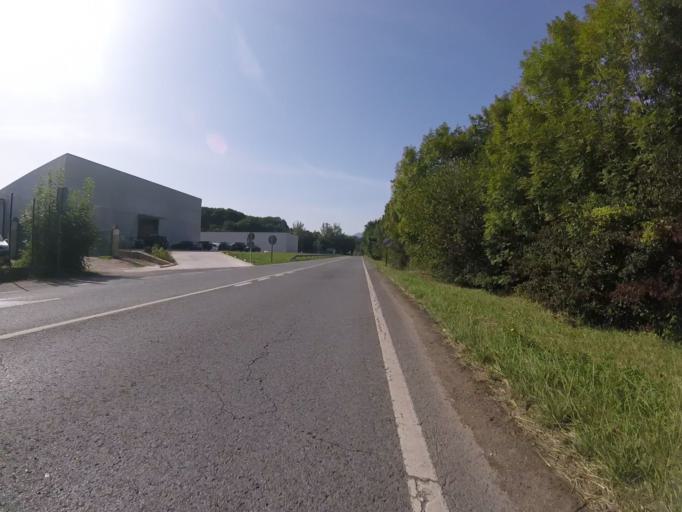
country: ES
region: Navarre
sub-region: Provincia de Navarra
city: Zugarramurdi
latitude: 43.1792
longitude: -1.4912
